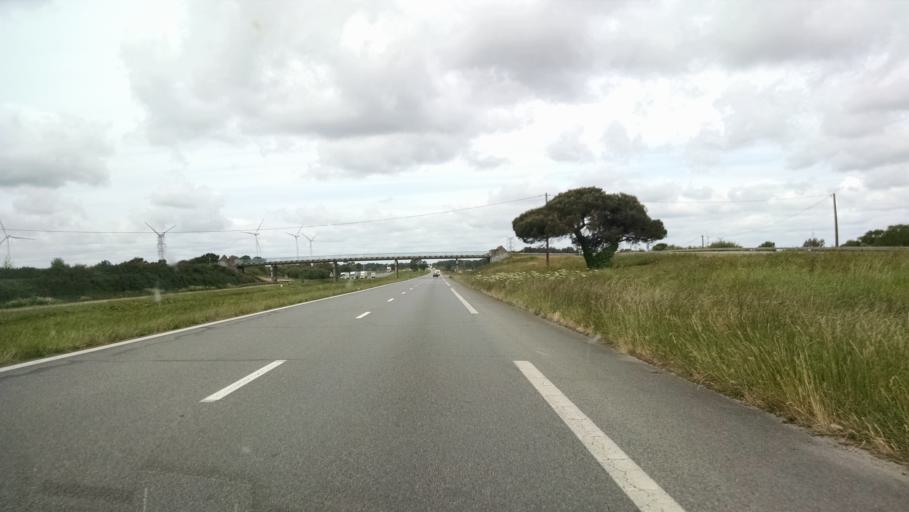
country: FR
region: Brittany
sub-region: Departement du Morbihan
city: Ambon
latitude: 47.5751
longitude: -2.5229
